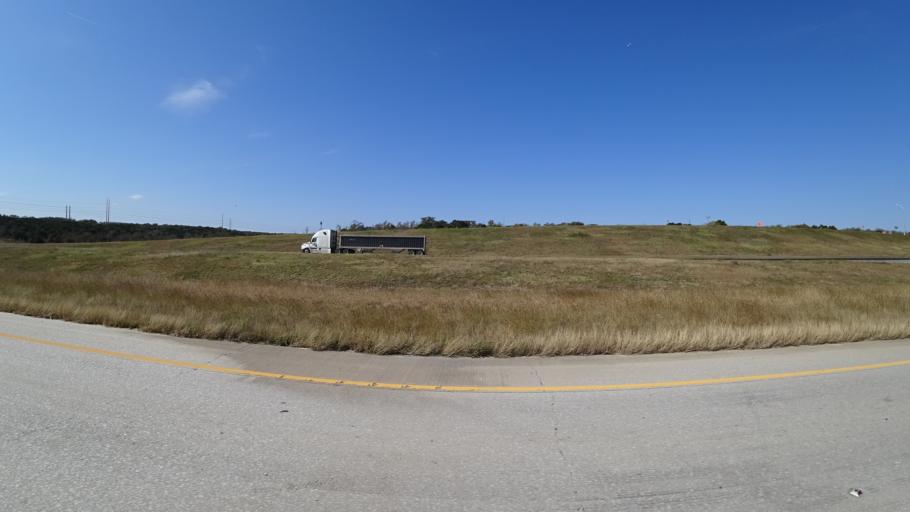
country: US
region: Texas
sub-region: Travis County
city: Manor
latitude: 30.2972
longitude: -97.5699
